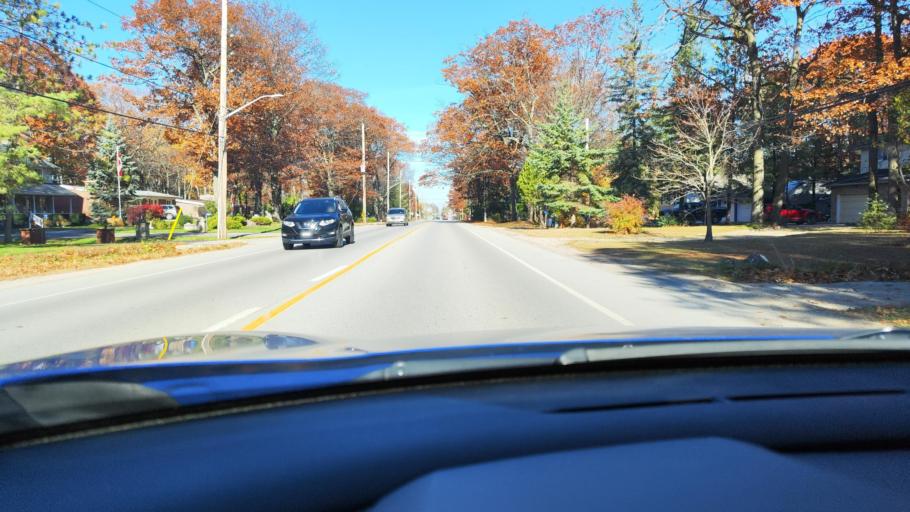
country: CA
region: Ontario
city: Wasaga Beach
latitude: 44.4653
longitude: -80.0740
